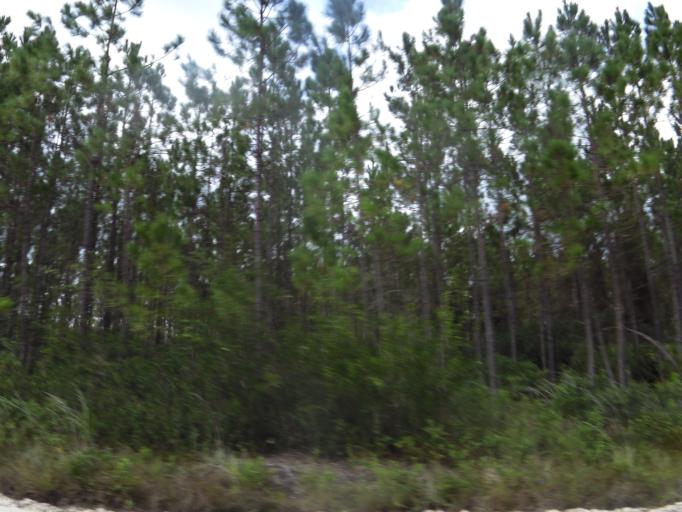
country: US
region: Florida
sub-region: Nassau County
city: Hilliard
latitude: 30.5935
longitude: -82.0499
